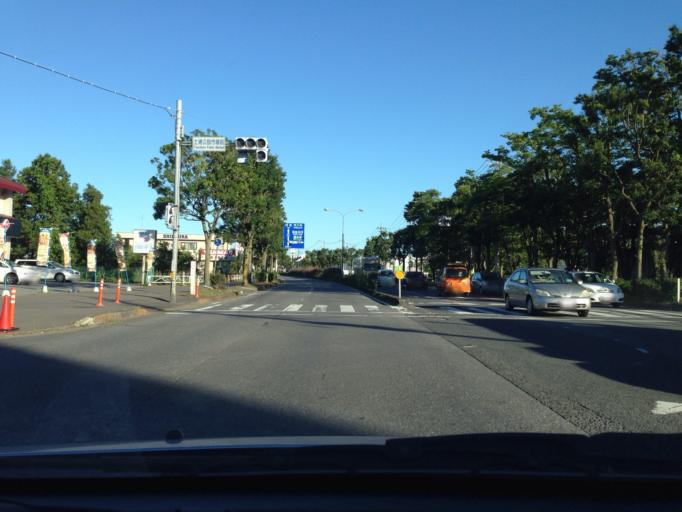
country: JP
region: Ibaraki
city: Naka
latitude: 36.0459
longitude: 140.1512
